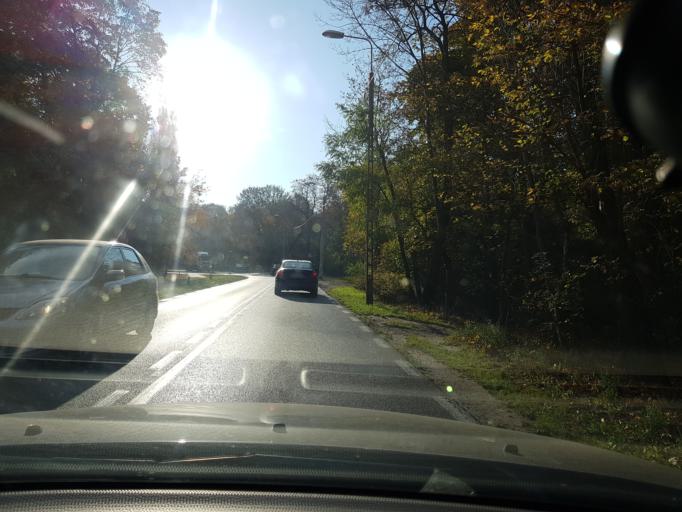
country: PL
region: Masovian Voivodeship
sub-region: Warszawa
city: Bemowo
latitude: 52.2645
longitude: 20.8848
